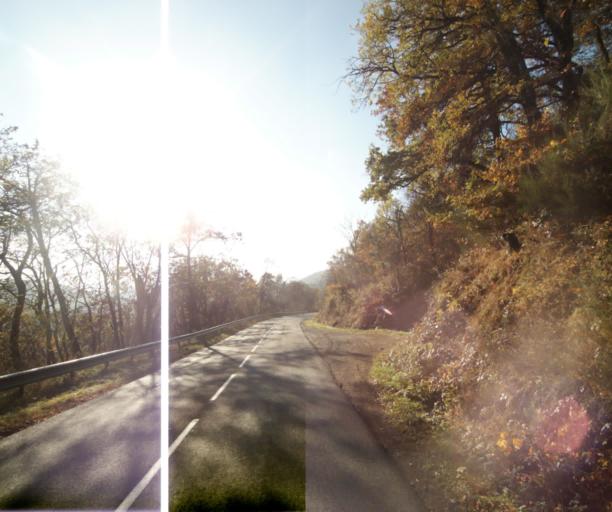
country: FR
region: Auvergne
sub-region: Departement du Puy-de-Dome
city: Nohanent
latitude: 45.8101
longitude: 3.0445
